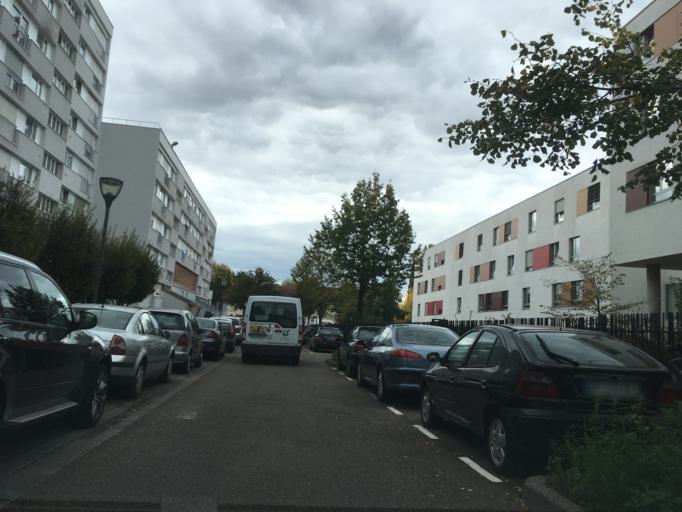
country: FR
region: Alsace
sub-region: Departement du Bas-Rhin
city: Strasbourg
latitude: 48.5554
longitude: 7.7657
